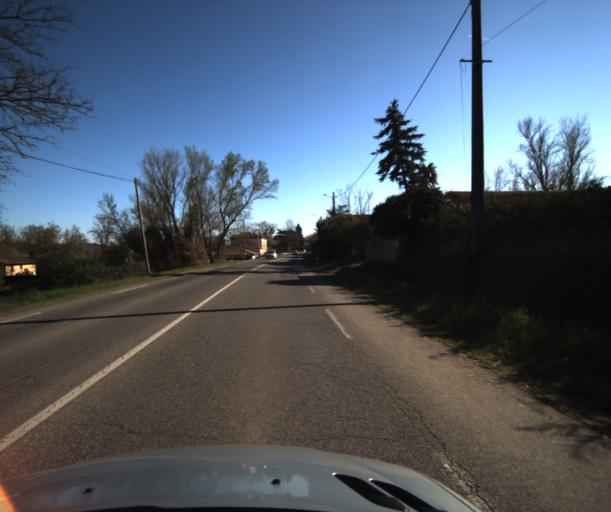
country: FR
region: Midi-Pyrenees
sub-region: Departement du Tarn-et-Garonne
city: Bressols
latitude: 43.9756
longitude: 1.3385
